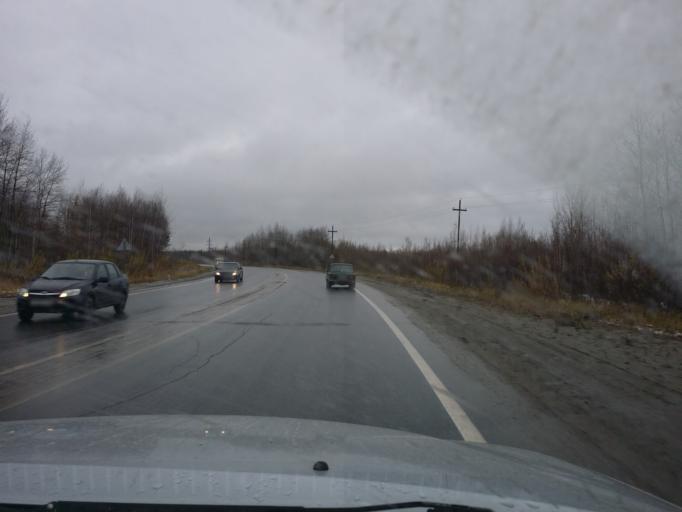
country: RU
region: Khanty-Mansiyskiy Avtonomnyy Okrug
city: Megion
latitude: 61.0852
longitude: 76.1151
